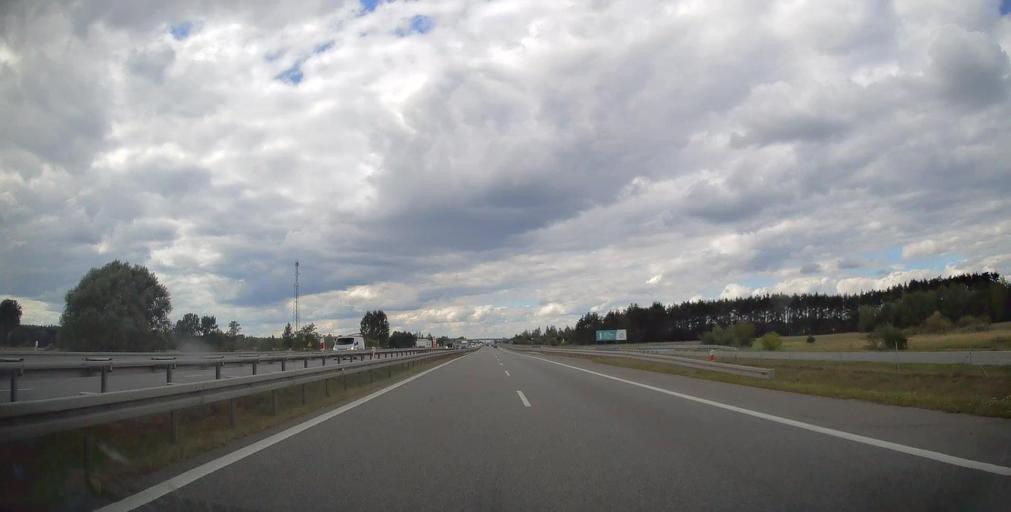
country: PL
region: Masovian Voivodeship
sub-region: Powiat radomski
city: Jedlinsk
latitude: 51.5403
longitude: 21.0648
